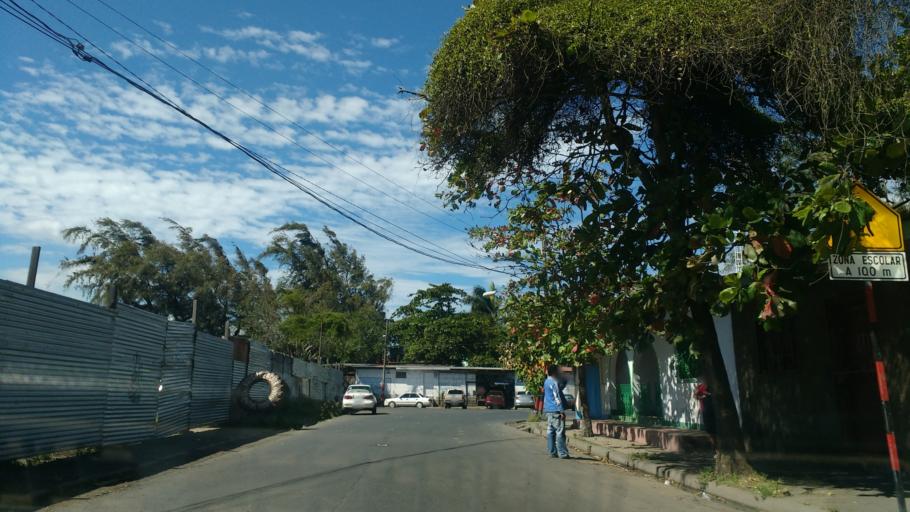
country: NI
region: Carazo
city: Diriamba
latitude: 11.8620
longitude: -86.2388
